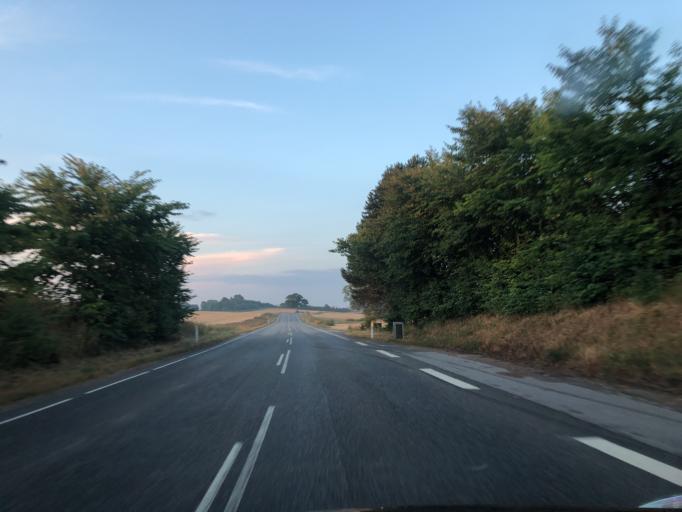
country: DK
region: Zealand
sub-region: Soro Kommune
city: Stenlille
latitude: 55.6067
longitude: 11.6549
